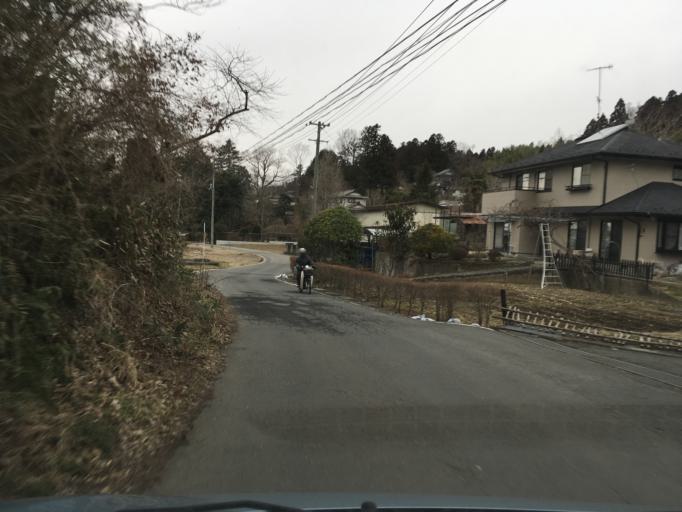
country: JP
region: Miyagi
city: Wakuya
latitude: 38.6653
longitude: 141.2804
